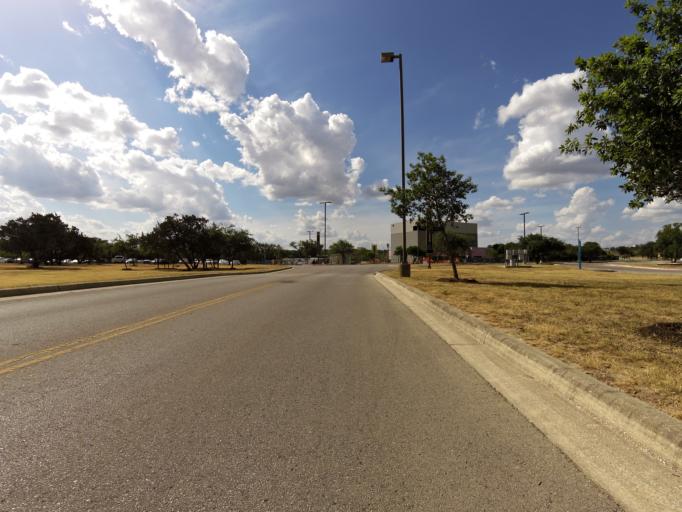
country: US
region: Texas
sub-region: Bexar County
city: Helotes
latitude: 29.5845
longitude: -98.6283
